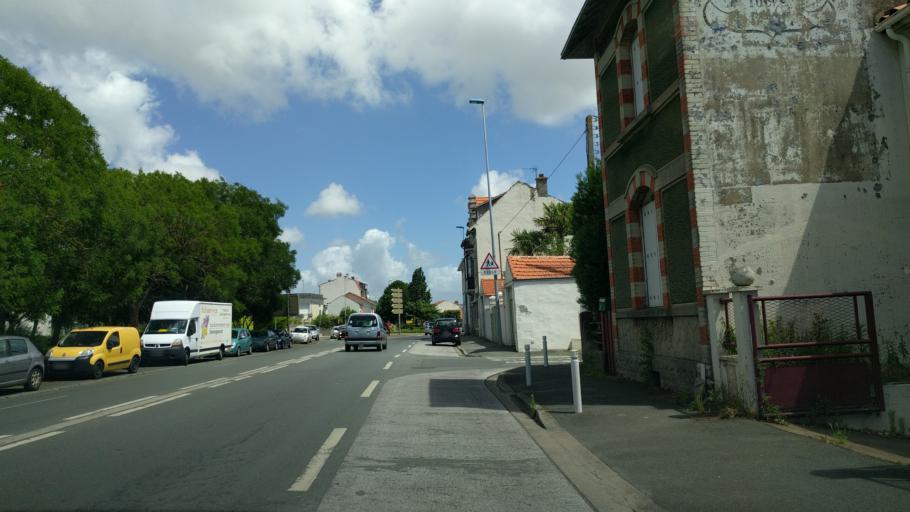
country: FR
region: Poitou-Charentes
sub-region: Departement de la Charente-Maritime
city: La Rochelle
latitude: 46.1607
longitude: -1.1404
